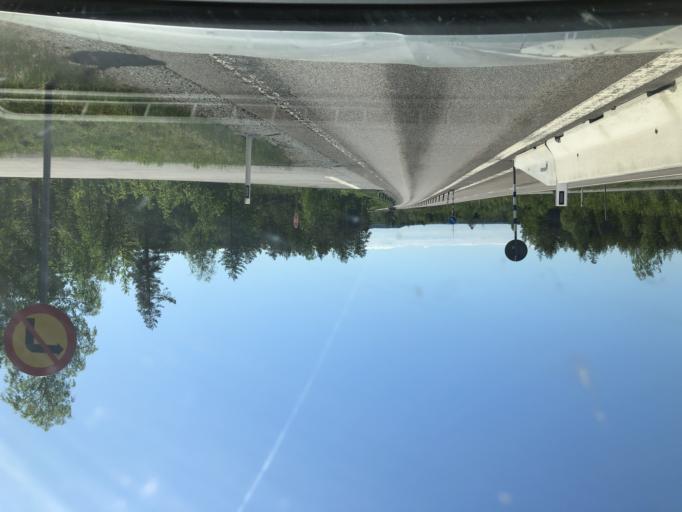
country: SE
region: Norrbotten
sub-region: Kalix Kommun
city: Toere
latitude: 65.9043
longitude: 22.8493
